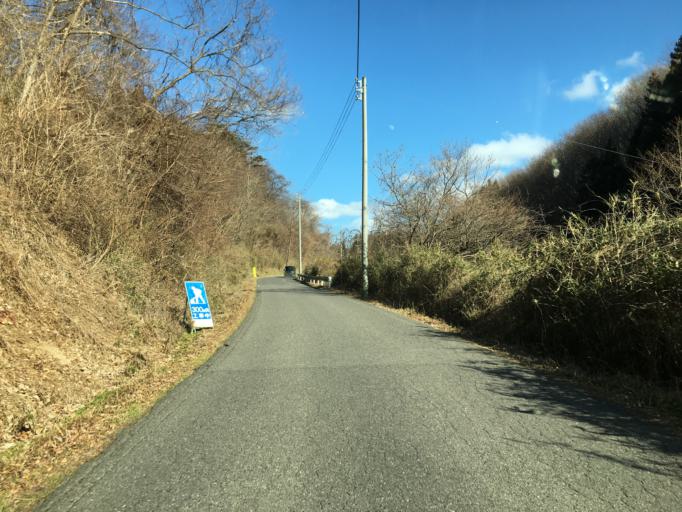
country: JP
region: Fukushima
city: Funehikimachi-funehiki
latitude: 37.4125
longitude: 140.5678
